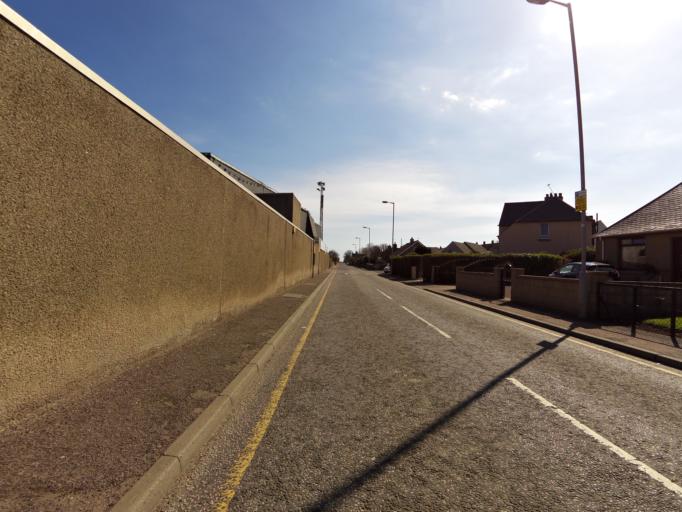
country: GB
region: Scotland
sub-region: Aberdeen City
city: Aberdeen
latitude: 57.1030
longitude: -2.0805
